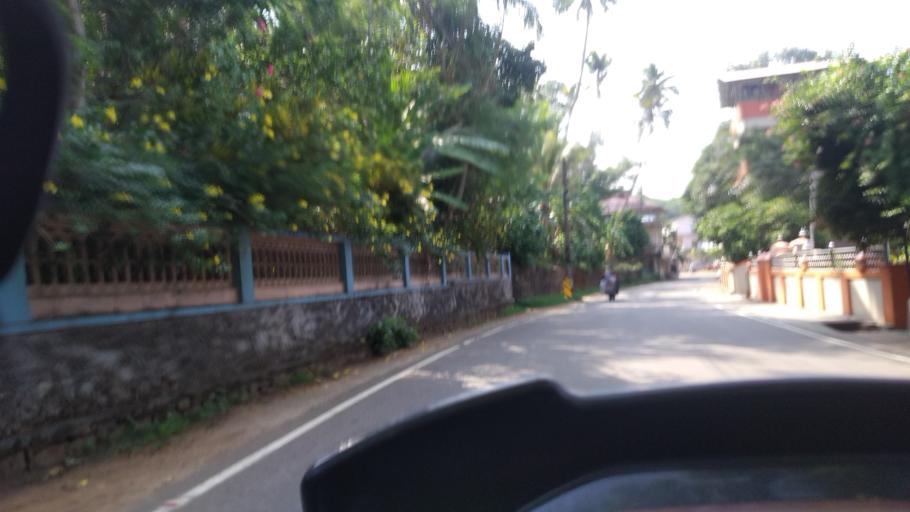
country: IN
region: Kerala
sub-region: Kottayam
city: Palackattumala
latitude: 9.8096
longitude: 76.5738
